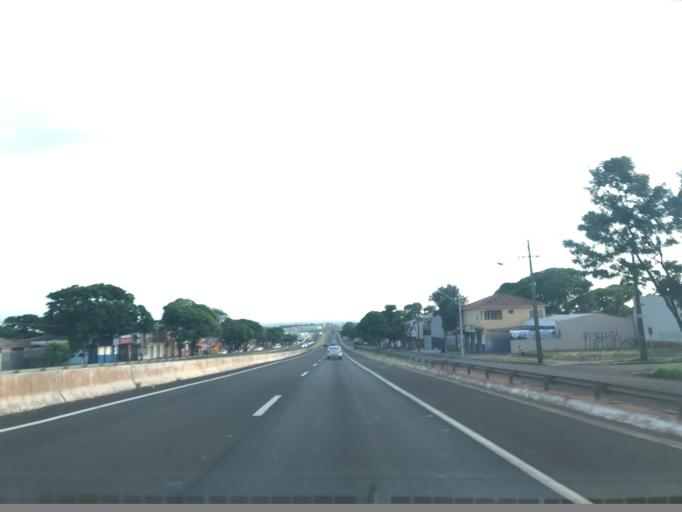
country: BR
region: Parana
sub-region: Maringa
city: Maringa
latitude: -23.3990
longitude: -51.9774
